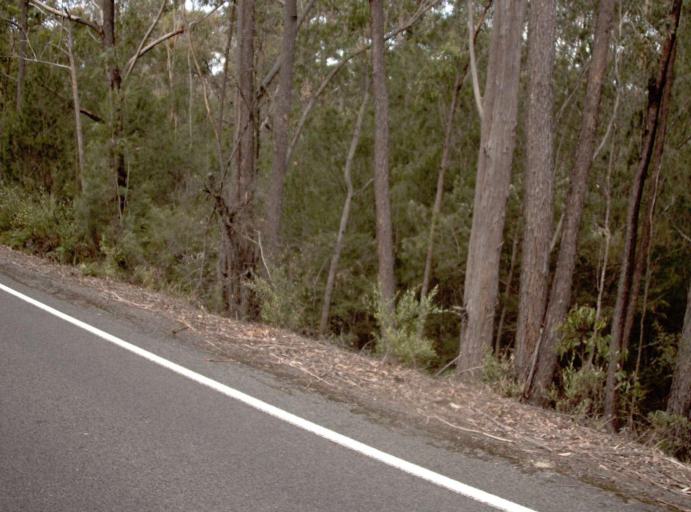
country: AU
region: New South Wales
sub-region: Bega Valley
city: Eden
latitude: -37.4945
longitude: 149.5489
